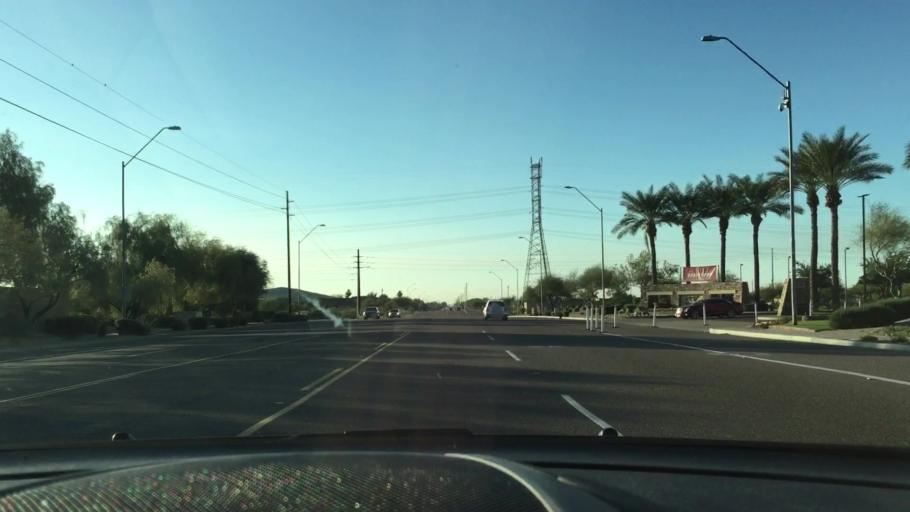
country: US
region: Arizona
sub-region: Maricopa County
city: Sun City
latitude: 33.7096
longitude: -112.2032
